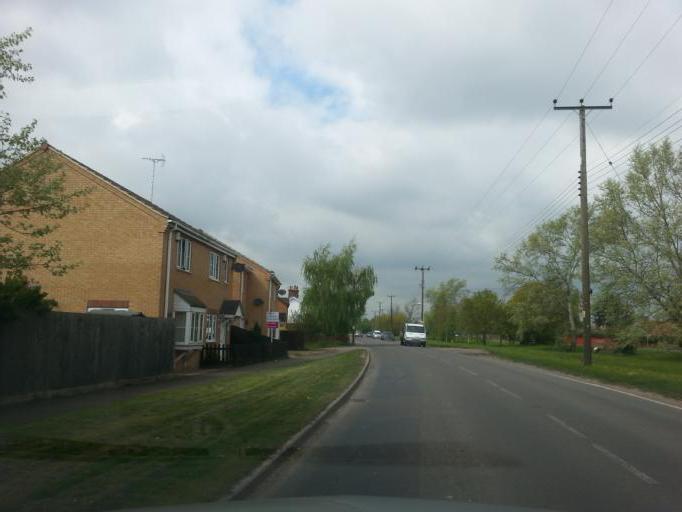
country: GB
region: England
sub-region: Norfolk
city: Outwell
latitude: 52.6156
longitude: 0.2317
